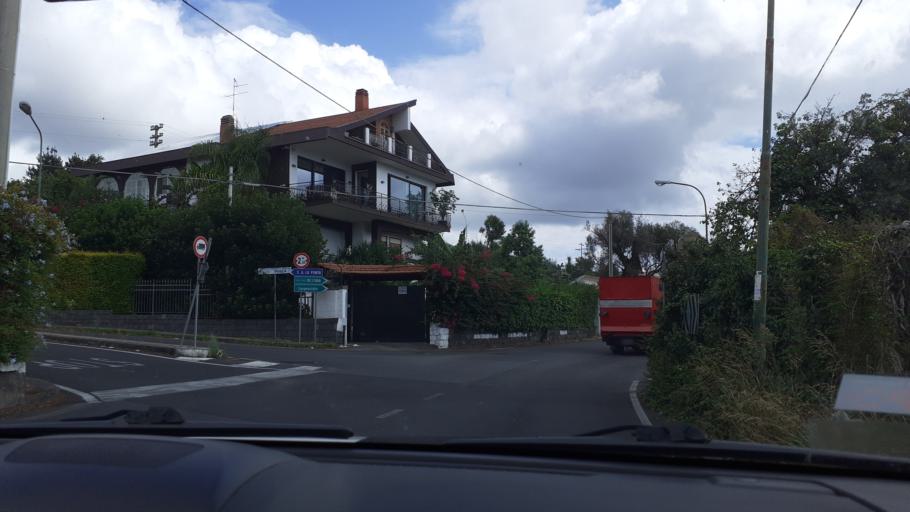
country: IT
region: Sicily
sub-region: Catania
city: Carrubazza-Motta
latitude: 37.5503
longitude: 15.1012
